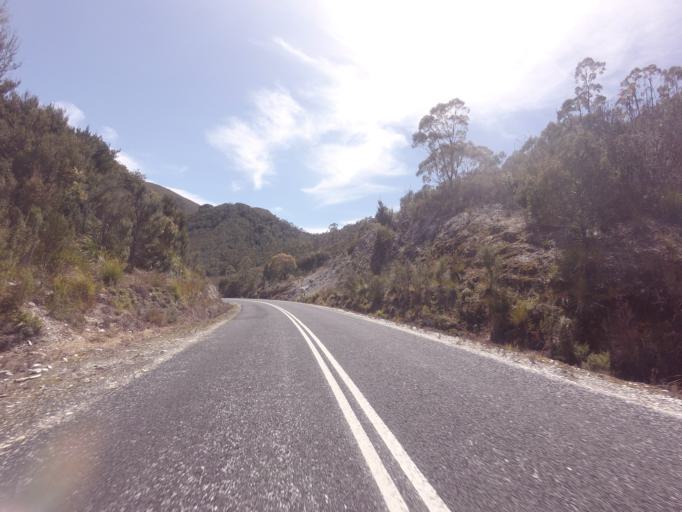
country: AU
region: Tasmania
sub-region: West Coast
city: Queenstown
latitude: -42.7952
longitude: 146.0863
